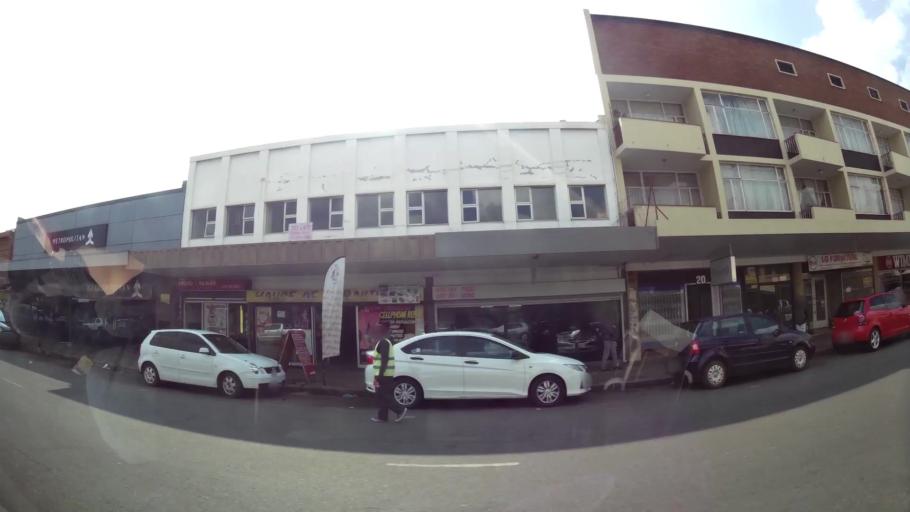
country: ZA
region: Gauteng
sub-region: Sedibeng District Municipality
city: Vereeniging
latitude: -26.6720
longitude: 27.9307
